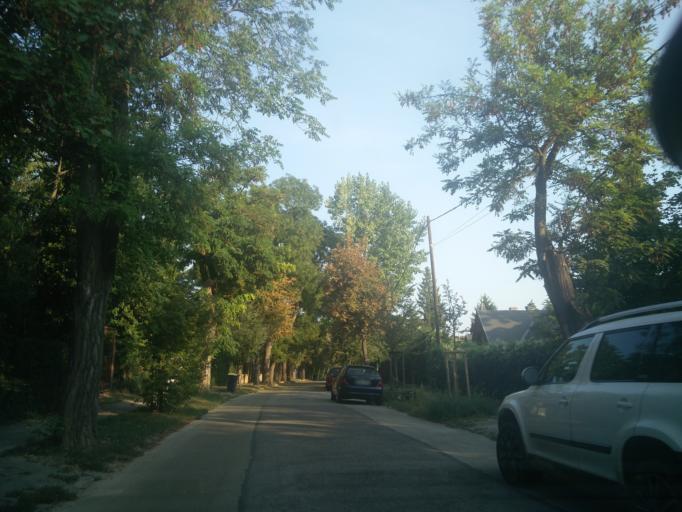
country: HU
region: Budapest
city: Budapest XII. keruelet
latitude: 47.4877
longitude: 19.0139
